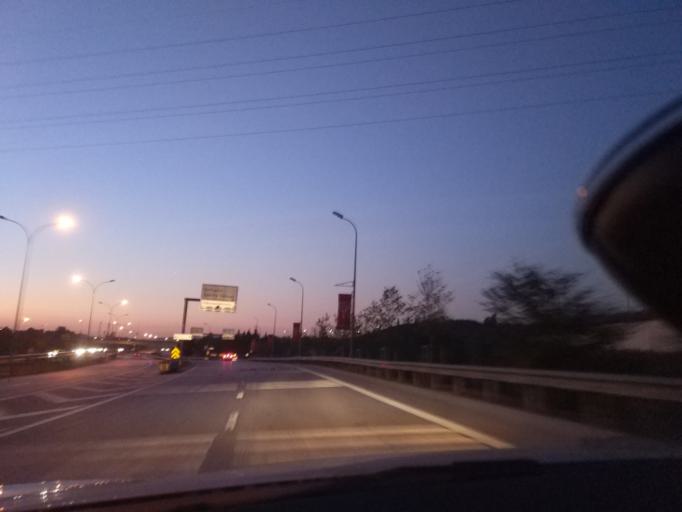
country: TR
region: Istanbul
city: Pendik
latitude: 40.9177
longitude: 29.3219
